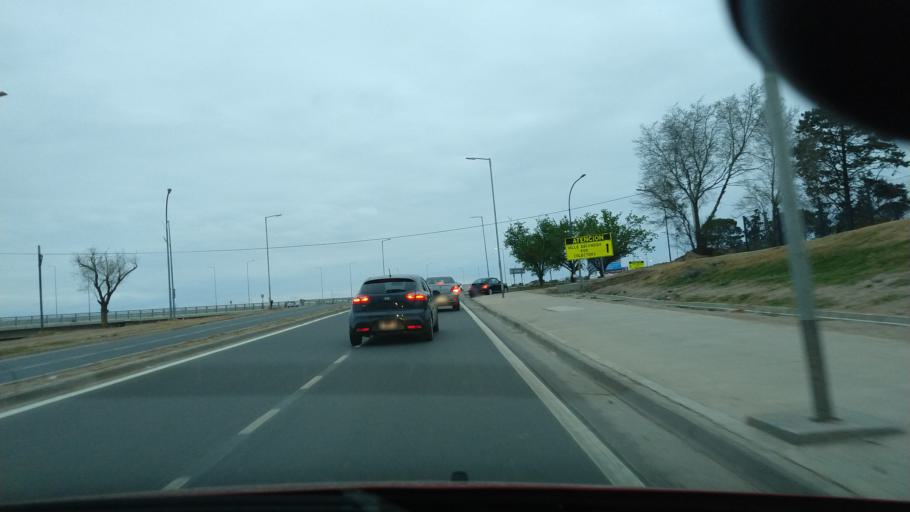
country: AR
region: Cordoba
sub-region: Departamento de Capital
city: Cordoba
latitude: -31.3713
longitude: -64.2532
